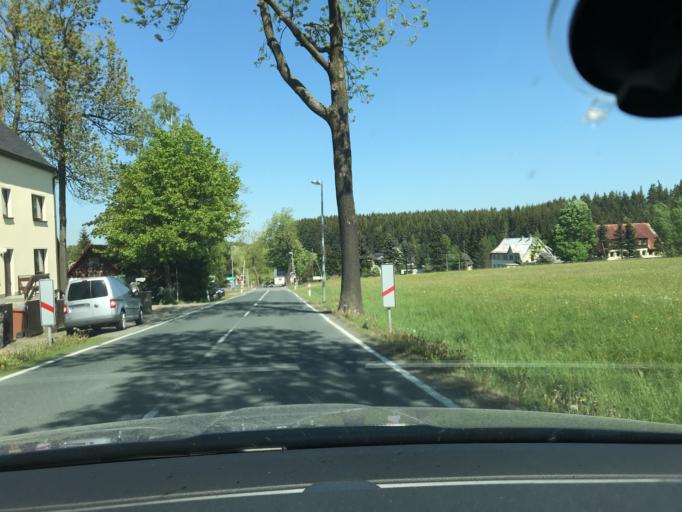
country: CZ
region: Ustecky
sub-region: Okres Chomutov
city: Vejprty
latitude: 50.4666
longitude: 12.9898
